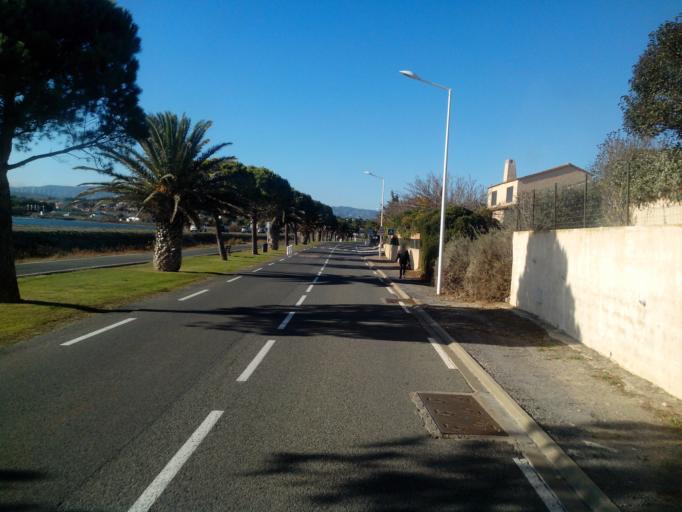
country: FR
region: Languedoc-Roussillon
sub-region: Departement de l'Aude
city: Leucate
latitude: 42.9048
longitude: 3.0452
